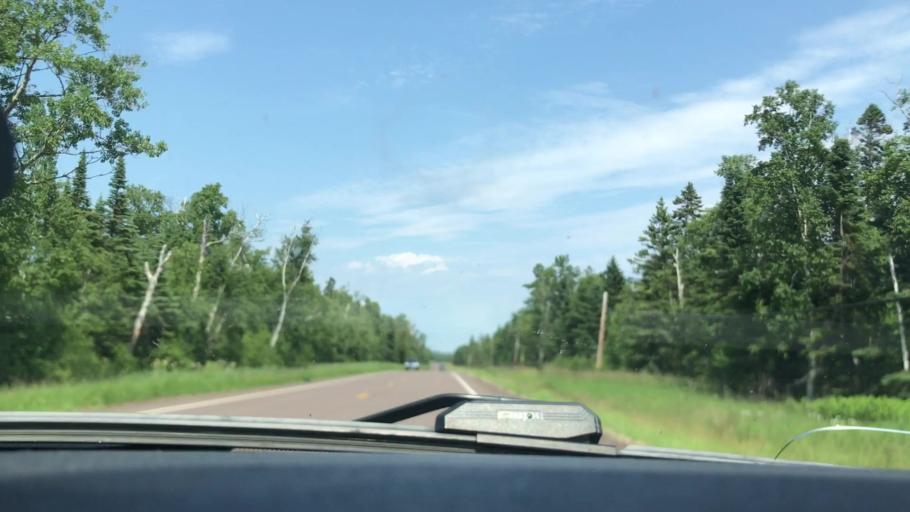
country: US
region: Minnesota
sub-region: Cook County
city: Grand Marais
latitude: 47.6323
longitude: -90.7225
